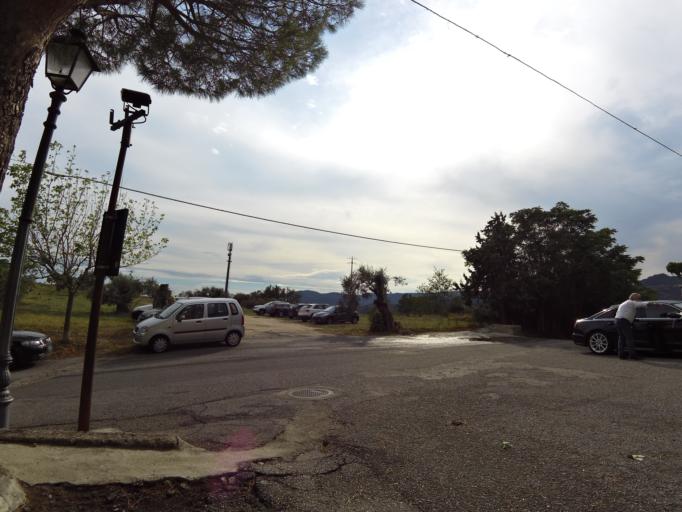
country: IT
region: Calabria
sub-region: Provincia di Reggio Calabria
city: Stignano
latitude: 38.4221
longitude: 16.4671
